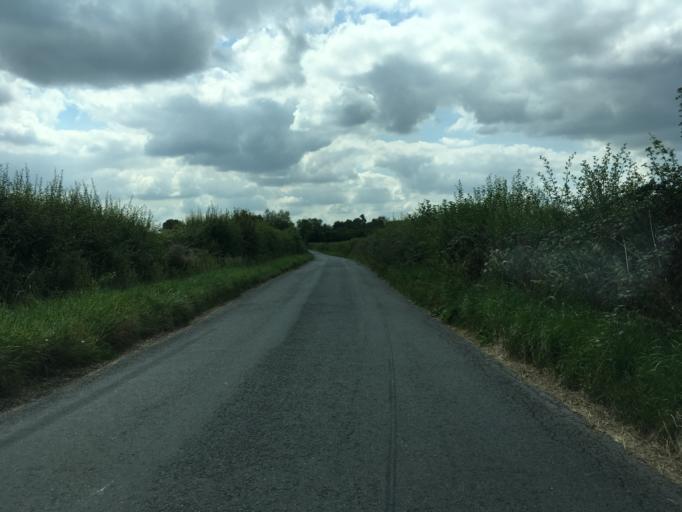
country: GB
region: England
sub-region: Gloucestershire
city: Gloucester
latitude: 51.9108
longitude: -2.2417
